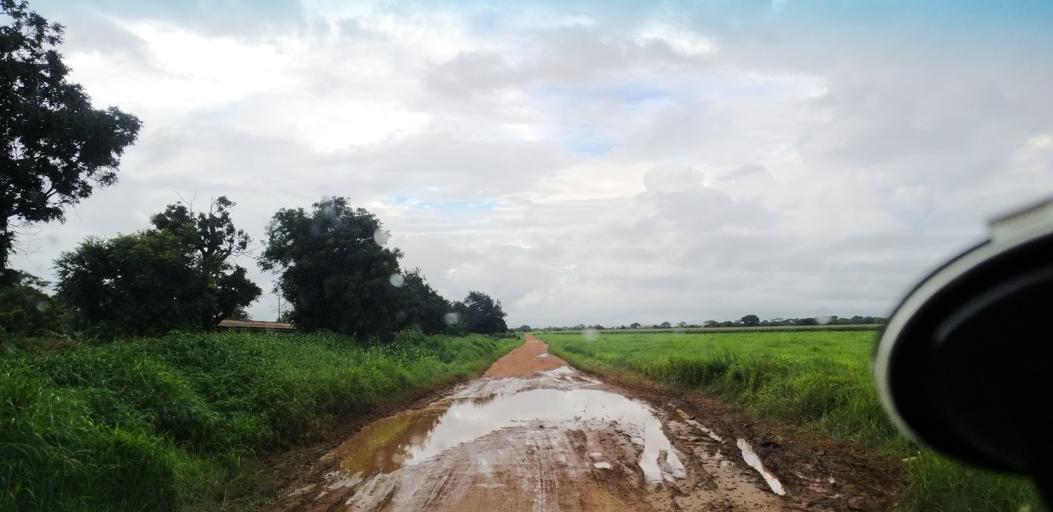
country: ZM
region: Lusaka
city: Lusaka
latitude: -15.5235
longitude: 28.2992
